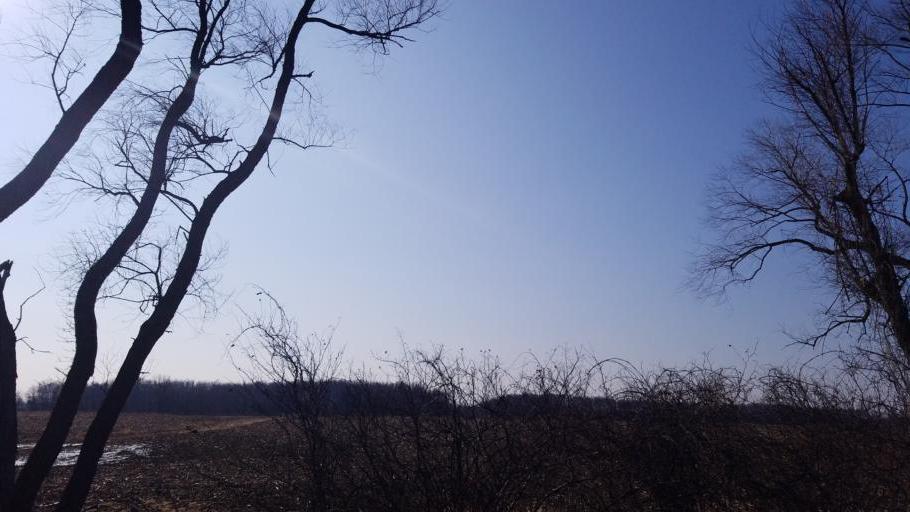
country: US
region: Ohio
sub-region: Morrow County
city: Mount Gilead
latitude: 40.6464
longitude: -82.8732
